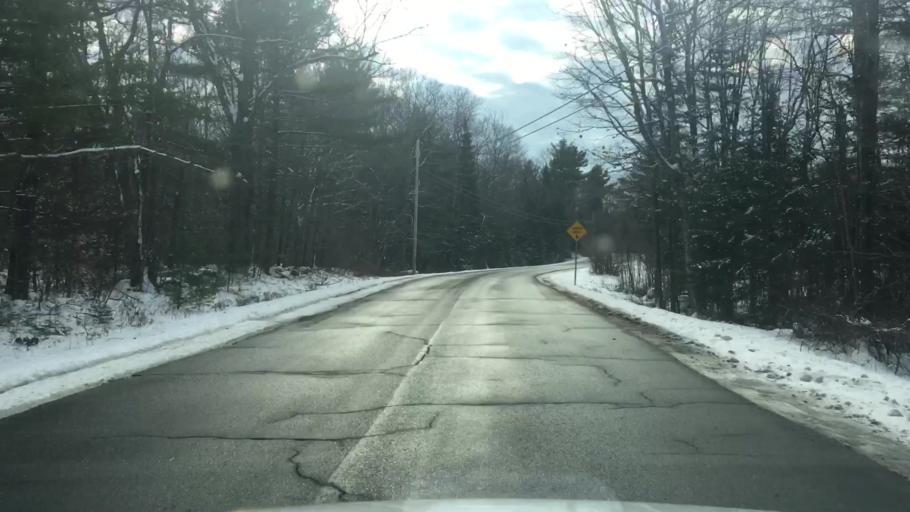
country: US
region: Maine
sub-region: Kennebec County
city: Chelsea
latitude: 44.2853
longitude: -69.6664
